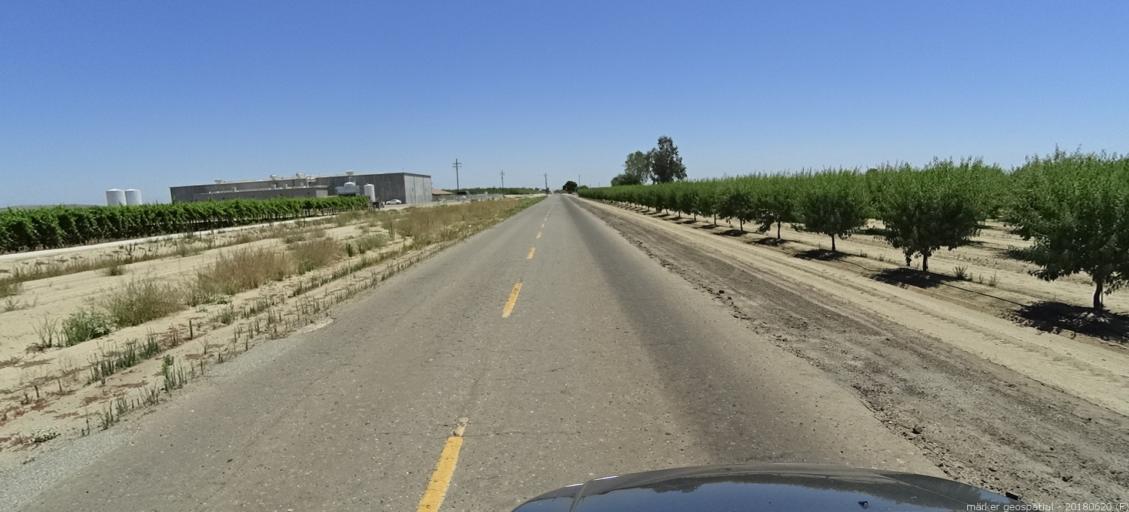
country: US
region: California
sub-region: Fresno County
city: Biola
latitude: 36.8657
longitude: -119.9865
